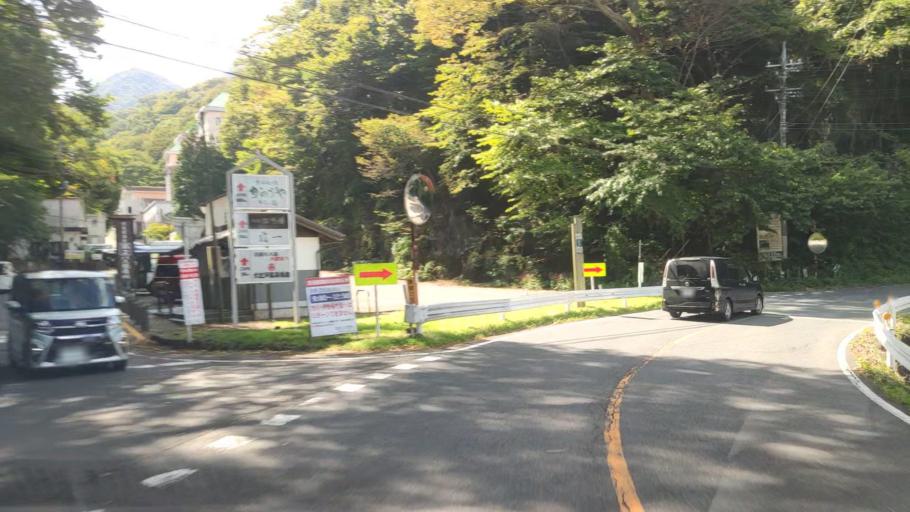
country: JP
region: Gunma
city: Shibukawa
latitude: 36.4981
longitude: 138.9152
